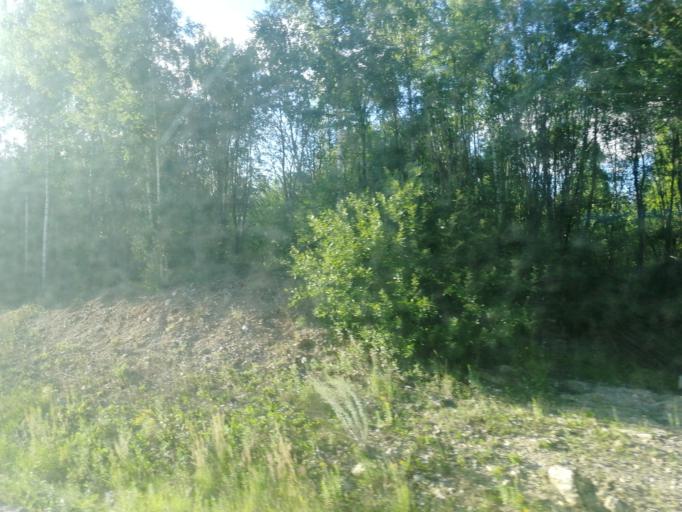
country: RU
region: Tula
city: Novogurovskiy
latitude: 54.2797
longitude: 37.2155
